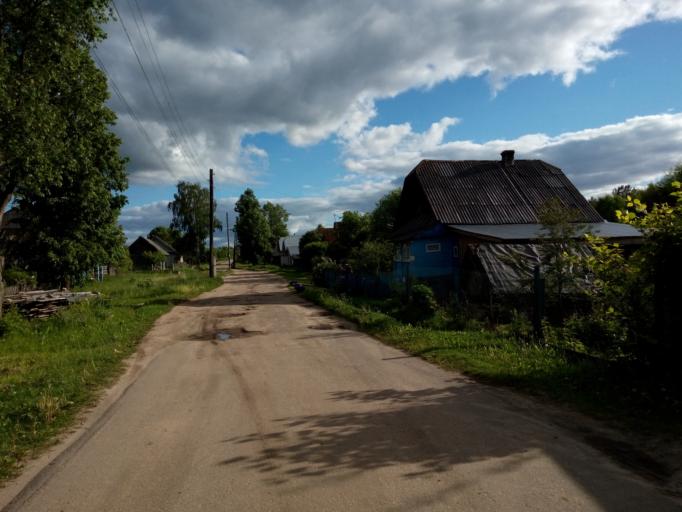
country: RU
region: Nizjnij Novgorod
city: Voskresenskoye
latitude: 56.7840
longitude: 45.5133
